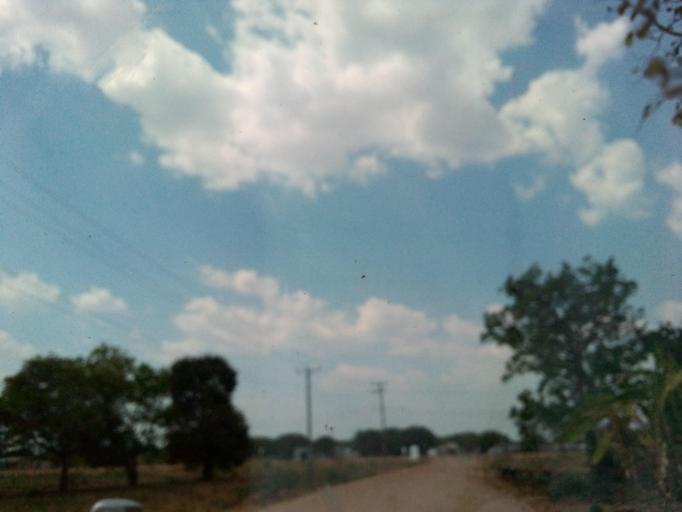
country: ZM
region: Northern
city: Mpika
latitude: -11.8369
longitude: 31.3838
